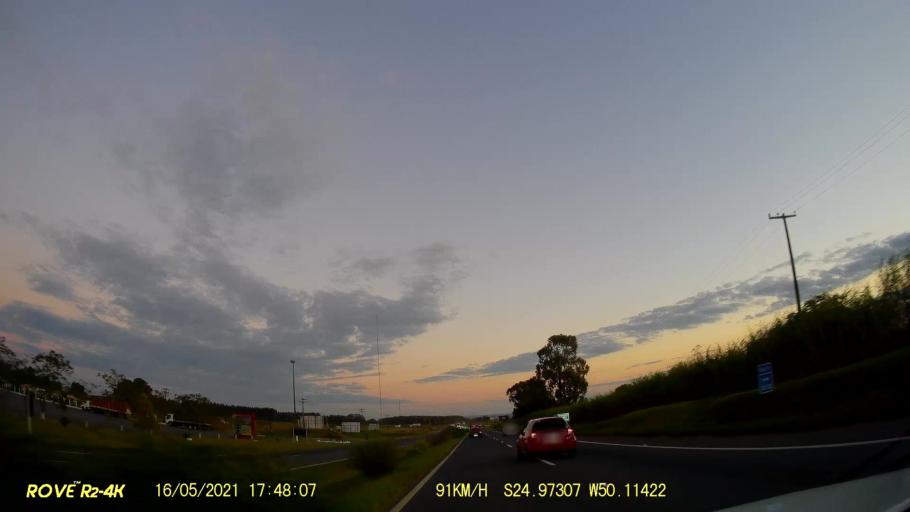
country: BR
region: Parana
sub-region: Carambei
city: Carambei
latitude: -24.9732
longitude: -50.1142
